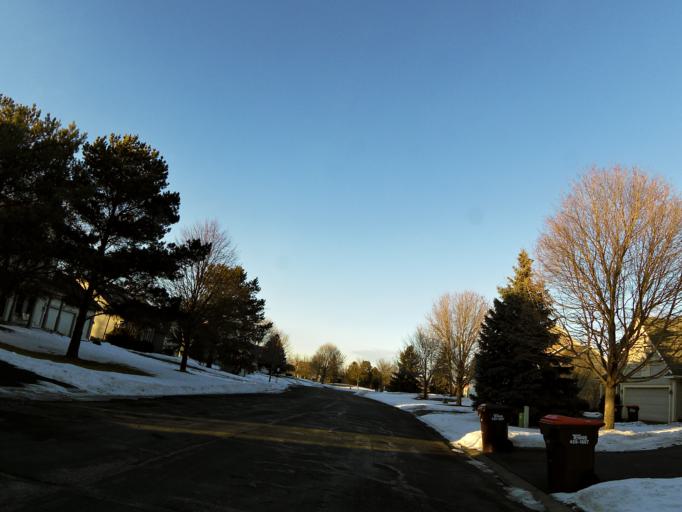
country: US
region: Minnesota
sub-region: Washington County
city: Woodbury
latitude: 44.8933
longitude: -92.8996
